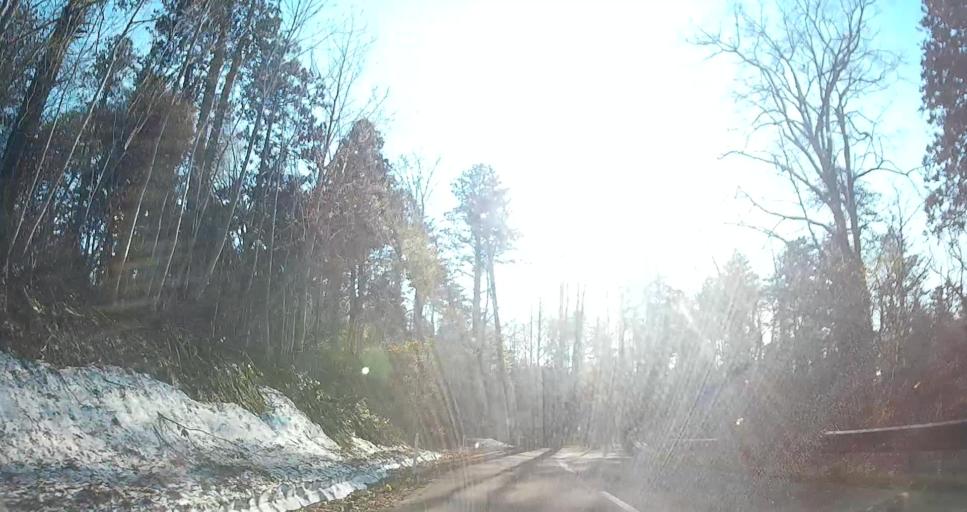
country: JP
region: Aomori
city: Mutsu
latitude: 41.3117
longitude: 141.1096
